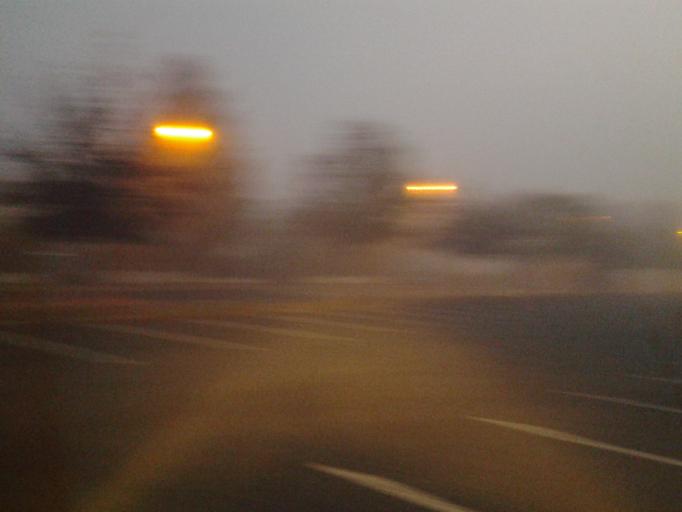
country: FR
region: Pays de la Loire
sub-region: Departement de la Vendee
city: Nesmy
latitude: 46.5827
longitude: -1.3726
